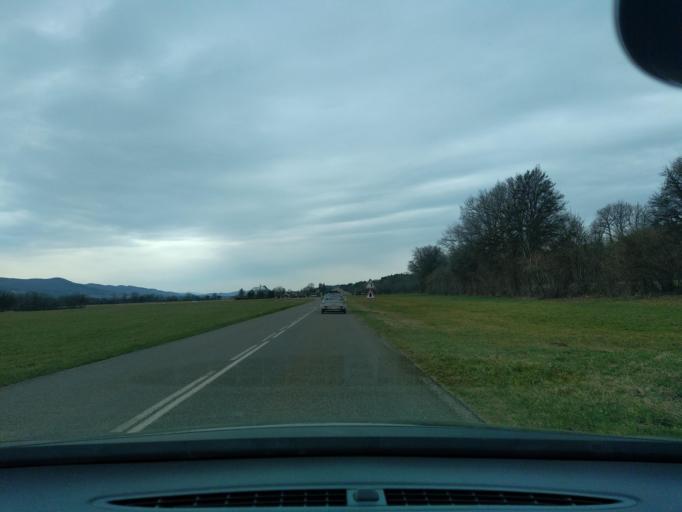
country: FR
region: Franche-Comte
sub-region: Departement du Jura
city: Arinthod
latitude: 46.4568
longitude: 5.5551
